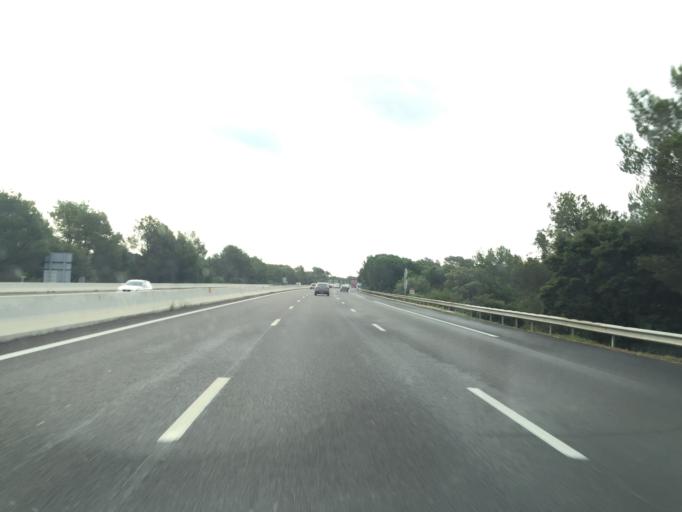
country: FR
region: Provence-Alpes-Cote d'Azur
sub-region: Departement du Var
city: Puget-sur-Argens
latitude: 43.4672
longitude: 6.6637
